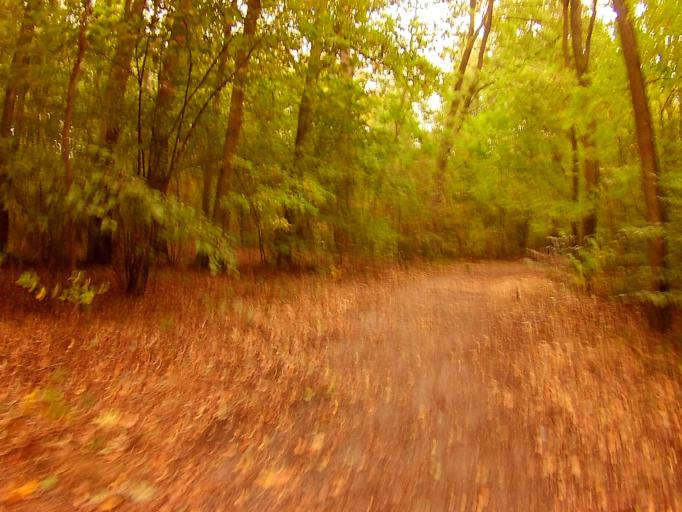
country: DE
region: Brandenburg
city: Zeuthen
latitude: 52.3922
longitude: 13.6268
